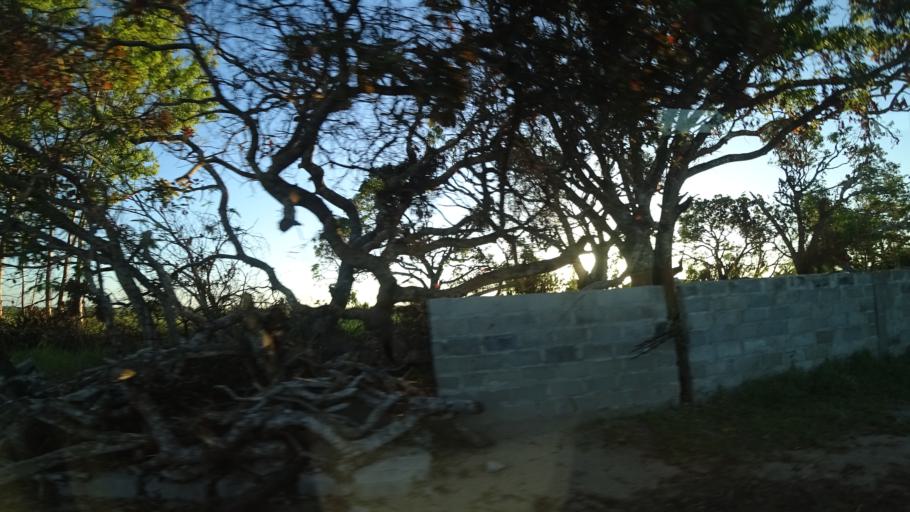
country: MZ
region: Sofala
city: Beira
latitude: -19.6210
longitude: 35.0606
